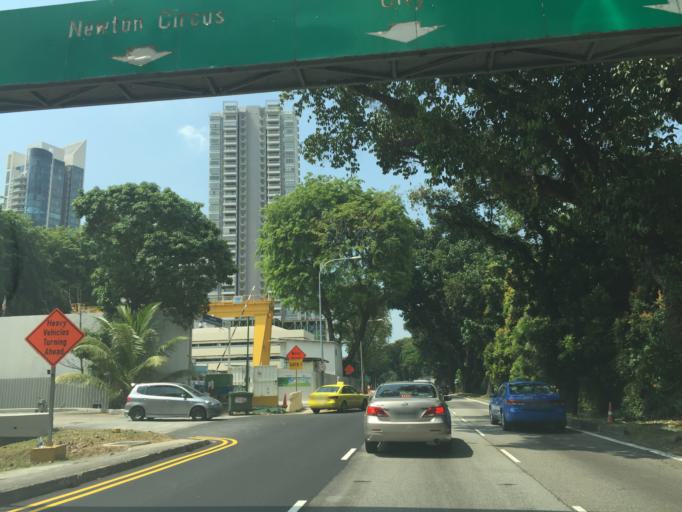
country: SG
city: Singapore
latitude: 1.3162
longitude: 103.8366
